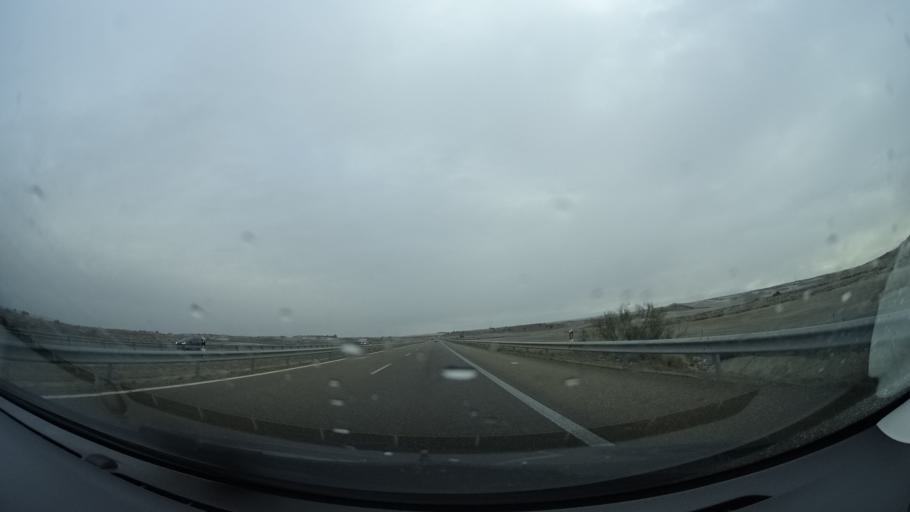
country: ES
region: Aragon
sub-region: Provincia de Huesca
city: Castejon de Monegros
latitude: 41.5223
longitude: -0.3195
